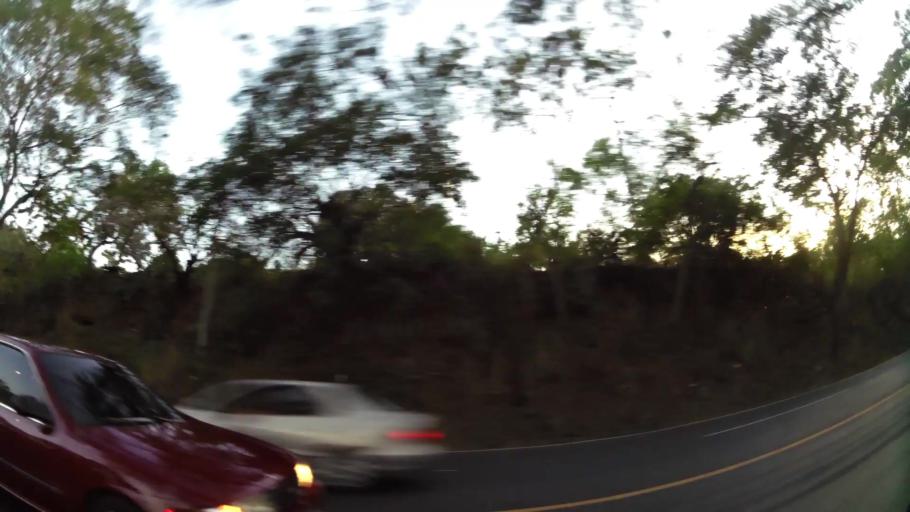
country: SV
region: San Miguel
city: San Miguel
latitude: 13.5019
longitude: -88.2184
